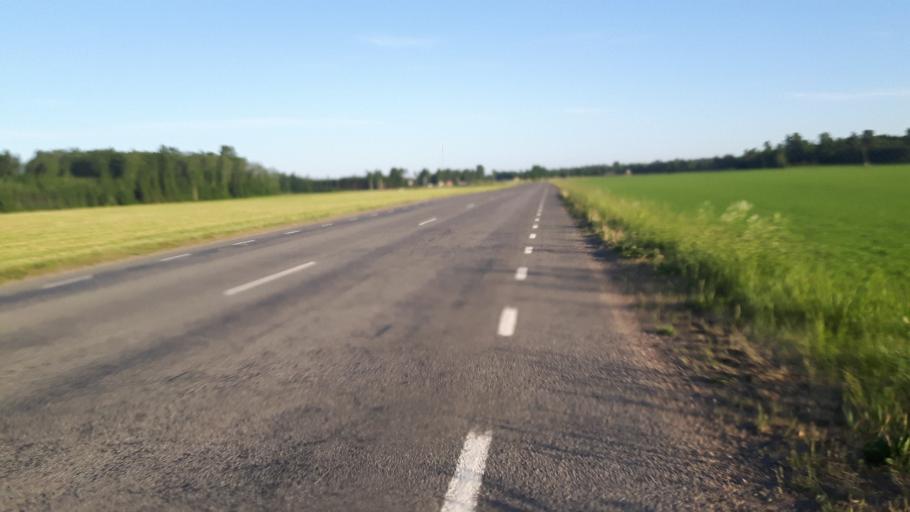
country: EE
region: Raplamaa
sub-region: Jaervakandi vald
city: Jarvakandi
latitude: 58.7768
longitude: 24.9442
